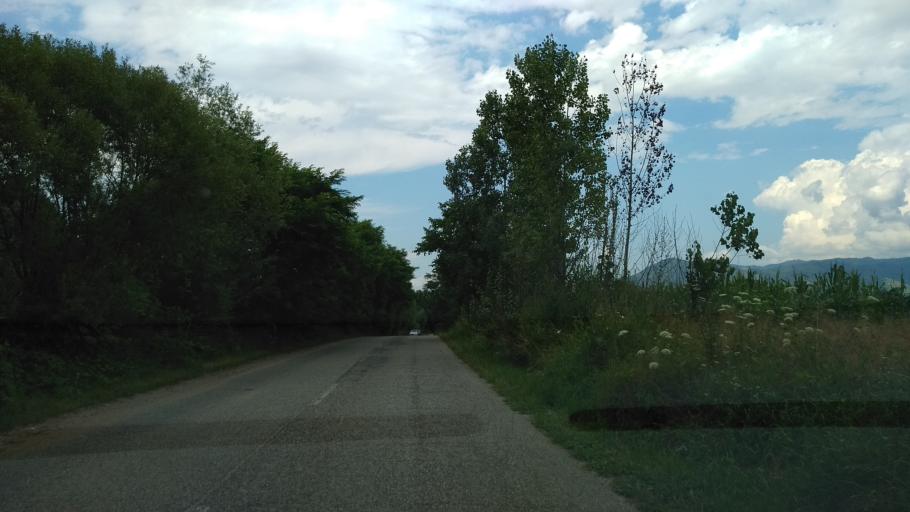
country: RO
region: Hunedoara
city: Salasu de Sus
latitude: 45.5037
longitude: 22.9501
